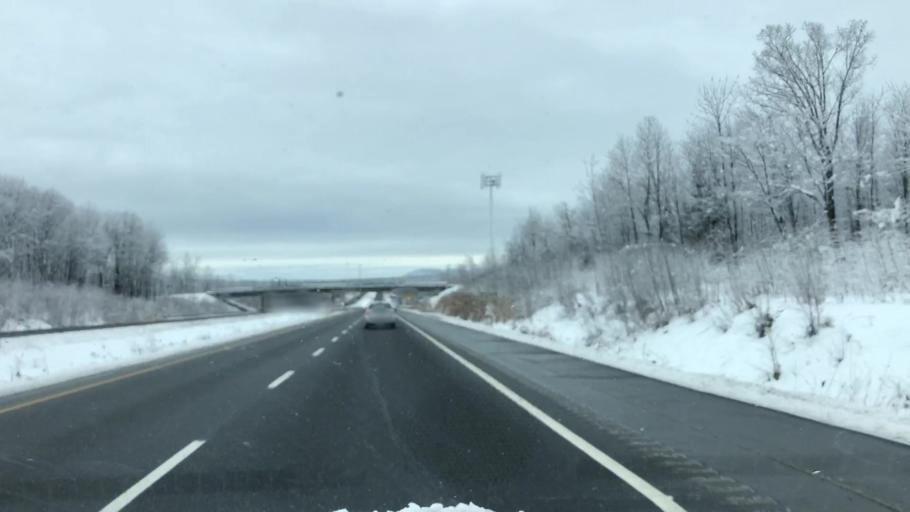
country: CA
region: Quebec
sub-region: Monteregie
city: Bromont
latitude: 45.3272
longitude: -72.6258
